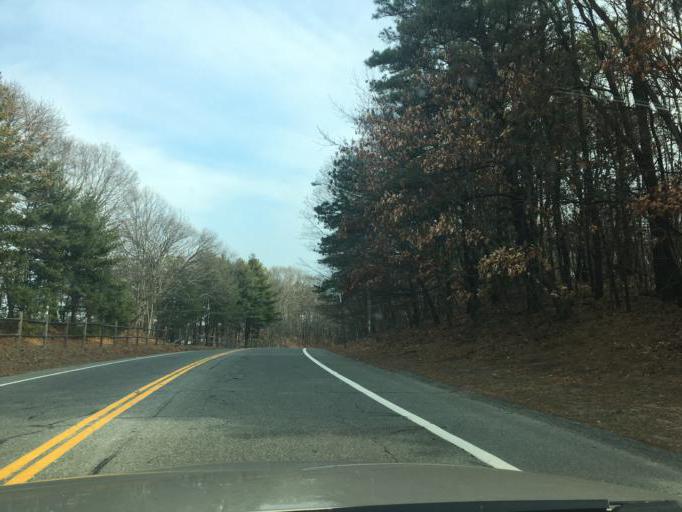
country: US
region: Rhode Island
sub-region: Providence County
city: East Providence
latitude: 41.8140
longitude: -71.3876
